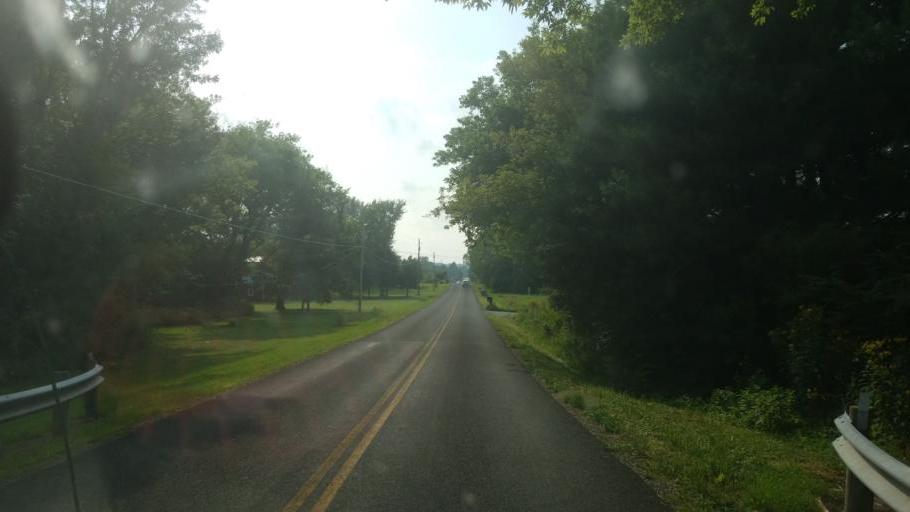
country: US
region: Ohio
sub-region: Medina County
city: Westfield Center
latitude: 41.0511
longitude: -81.8921
